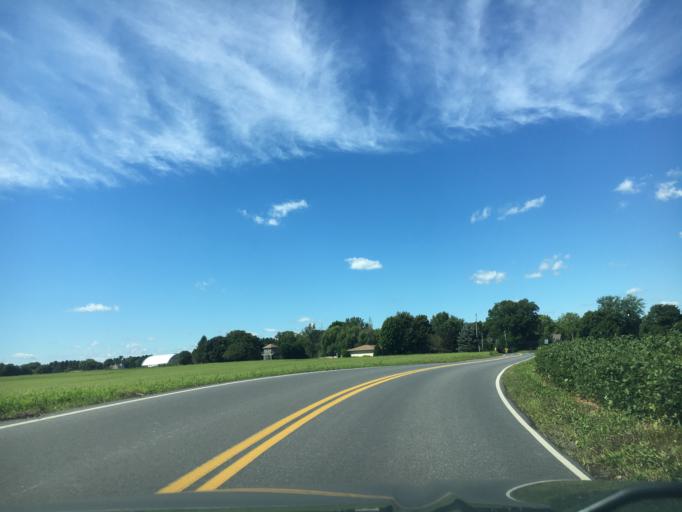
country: US
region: Pennsylvania
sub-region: Berks County
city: Topton
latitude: 40.5141
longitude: -75.6884
